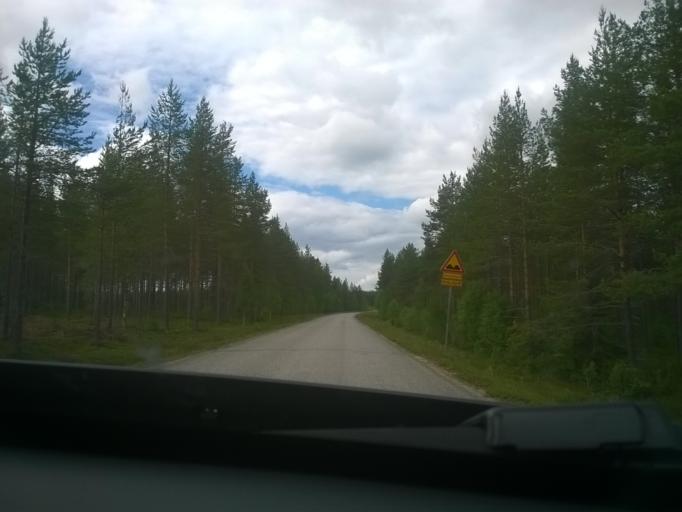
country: FI
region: Kainuu
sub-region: Kehys-Kainuu
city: Kuhmo
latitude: 64.3854
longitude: 29.8003
